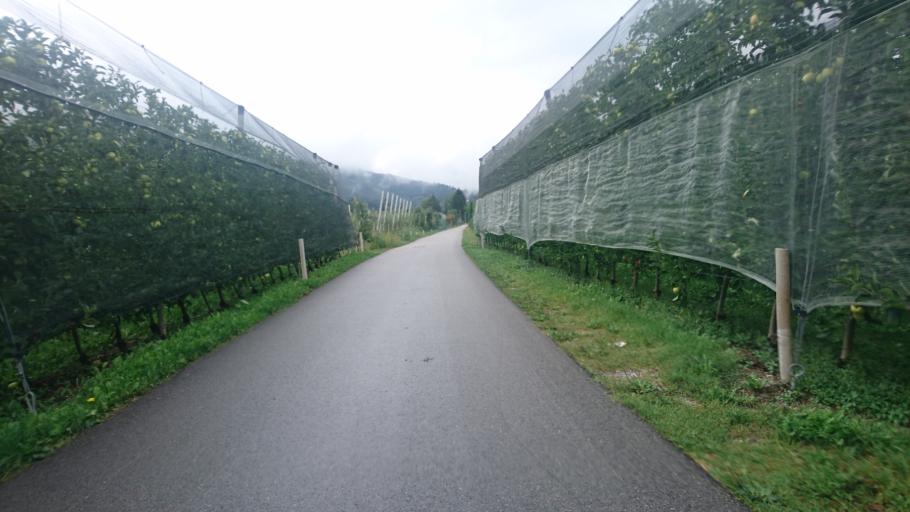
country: IT
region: Trentino-Alto Adige
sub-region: Provincia di Trento
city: Caldonazzo
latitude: 45.9911
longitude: 11.2738
